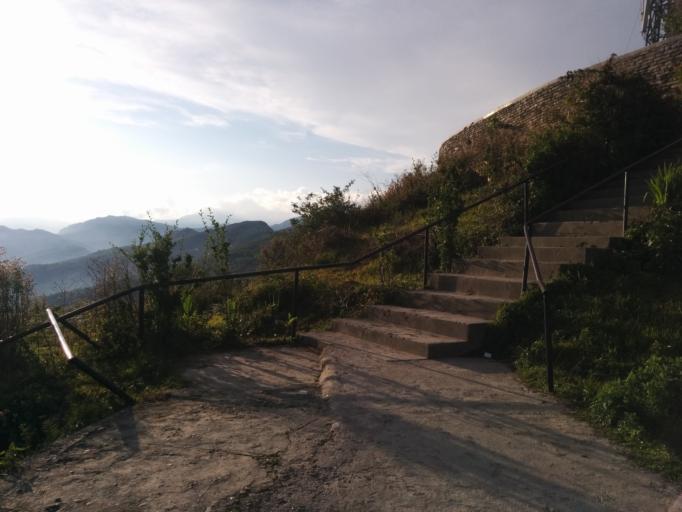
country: NP
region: Western Region
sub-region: Gandaki Zone
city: Pokhara
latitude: 28.2459
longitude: 83.9487
